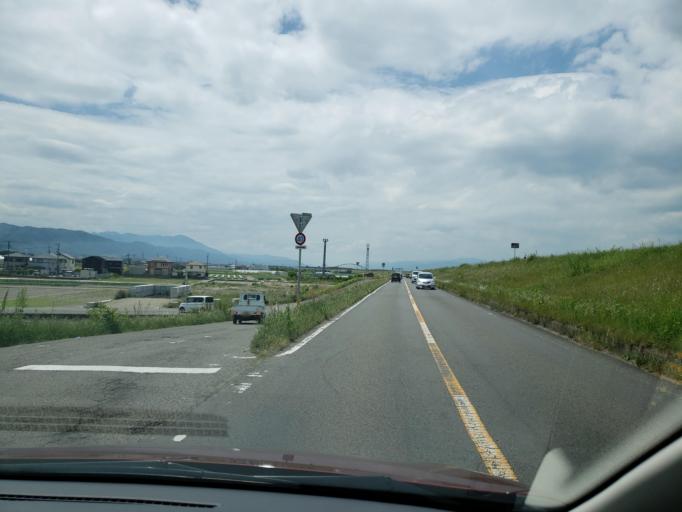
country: JP
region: Tokushima
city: Ishii
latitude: 34.0897
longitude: 134.4065
